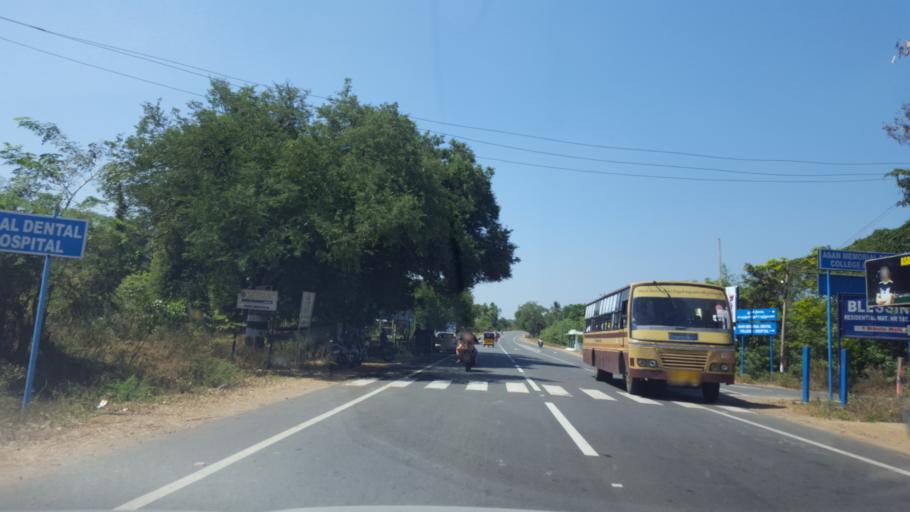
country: IN
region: Tamil Nadu
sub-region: Kancheepuram
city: Chengalpattu
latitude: 12.6481
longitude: 80.0381
